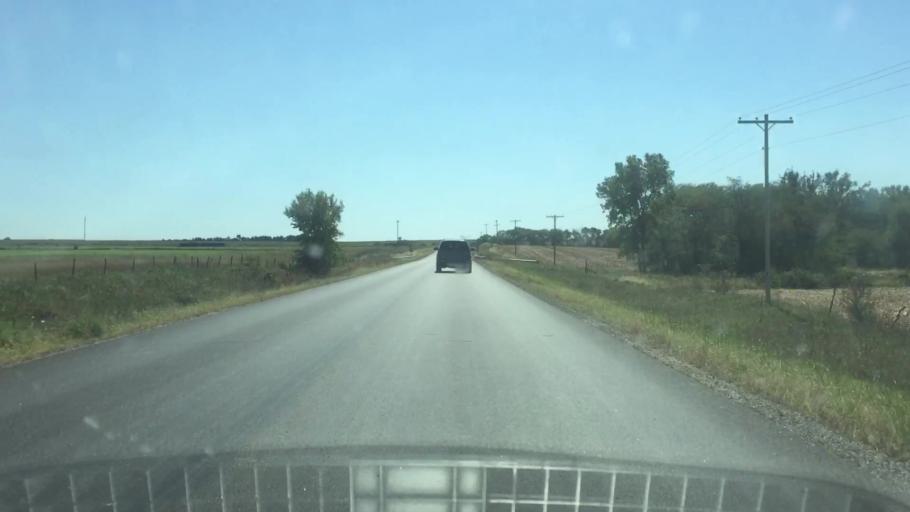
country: US
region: Kansas
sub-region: Marshall County
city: Marysville
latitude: 39.8825
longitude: -96.6010
